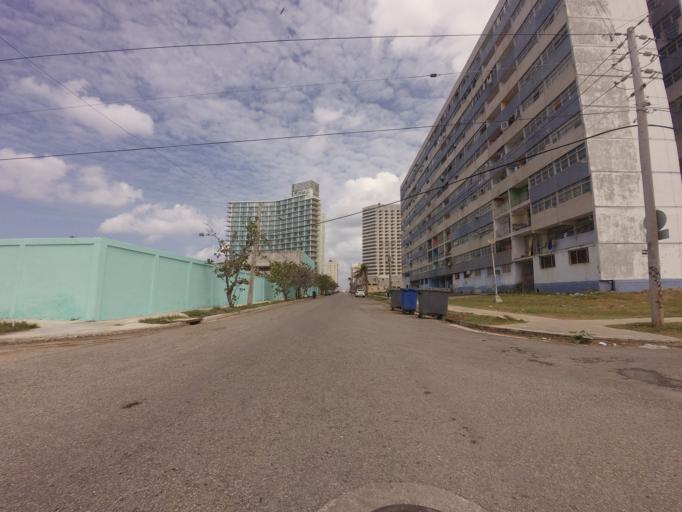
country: CU
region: La Habana
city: Havana
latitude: 23.1384
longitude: -82.4053
